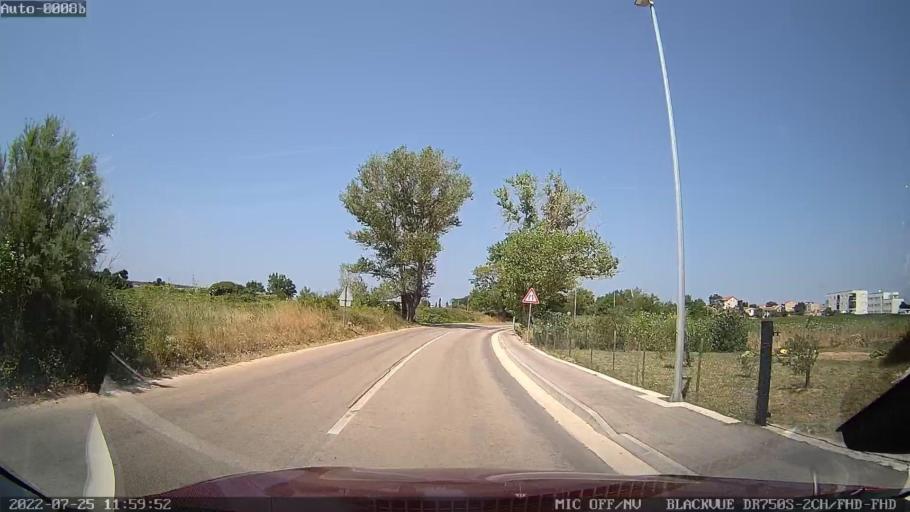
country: HR
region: Zadarska
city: Nin
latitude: 44.2424
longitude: 15.1976
